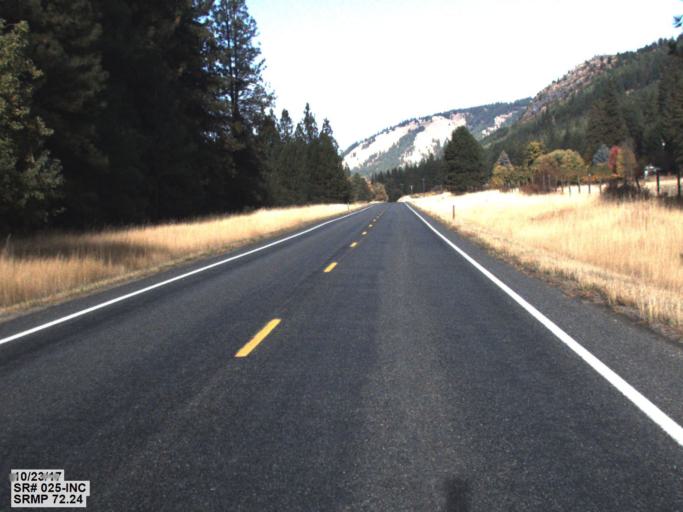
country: US
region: Washington
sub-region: Stevens County
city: Kettle Falls
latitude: 48.5042
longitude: -118.1541
